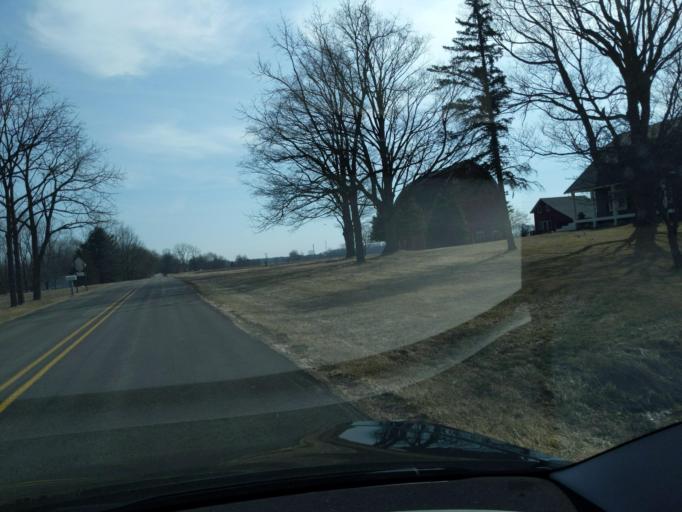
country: US
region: Michigan
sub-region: Ingham County
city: Webberville
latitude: 42.6592
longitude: -84.2260
